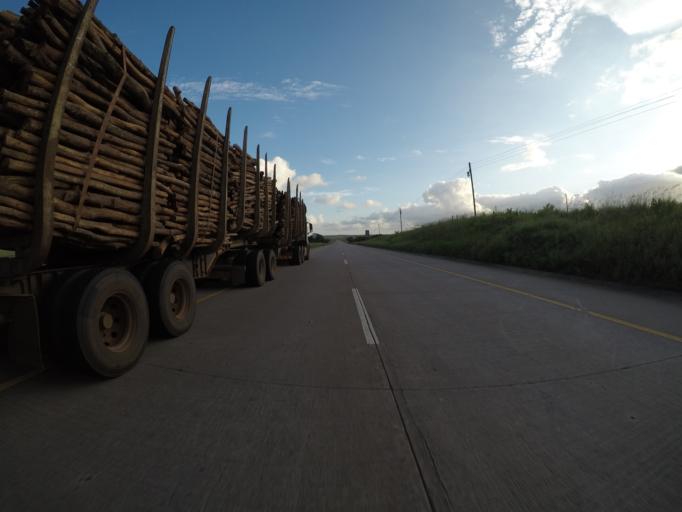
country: ZA
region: KwaZulu-Natal
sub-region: uMkhanyakude District Municipality
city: Mtubatuba
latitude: -28.4891
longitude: 32.1414
